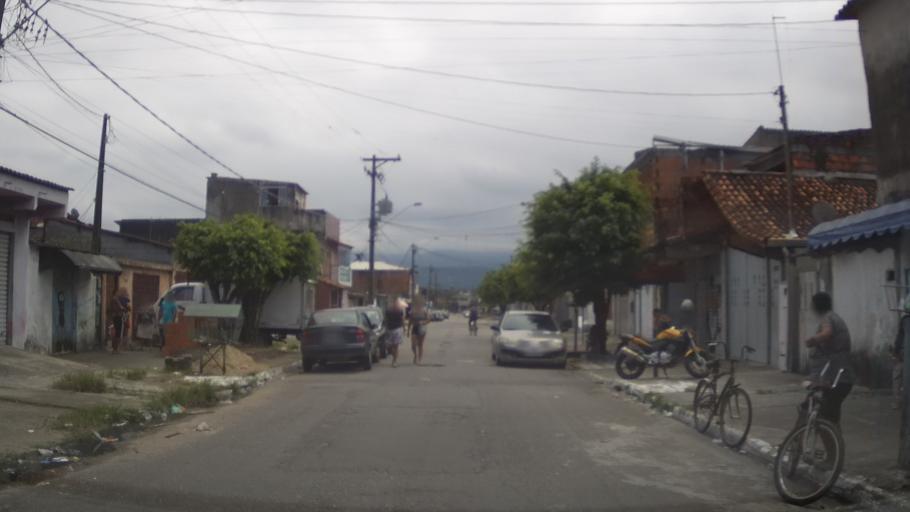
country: BR
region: Sao Paulo
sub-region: Praia Grande
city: Praia Grande
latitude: -24.0175
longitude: -46.4880
